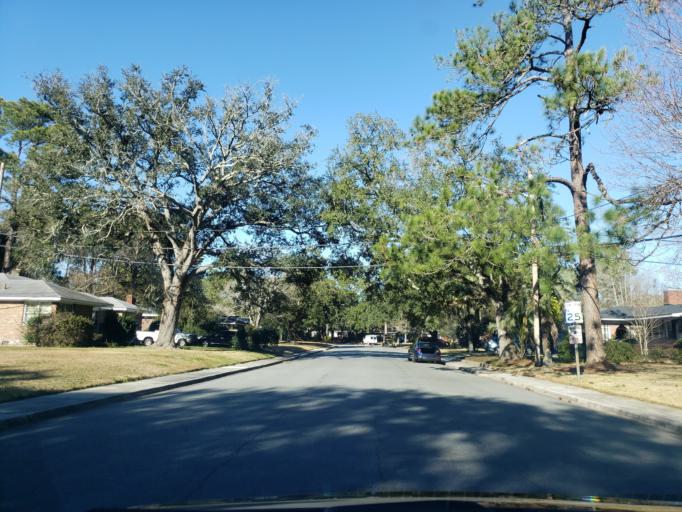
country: US
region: Georgia
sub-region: Chatham County
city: Thunderbolt
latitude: 32.0223
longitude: -81.0969
